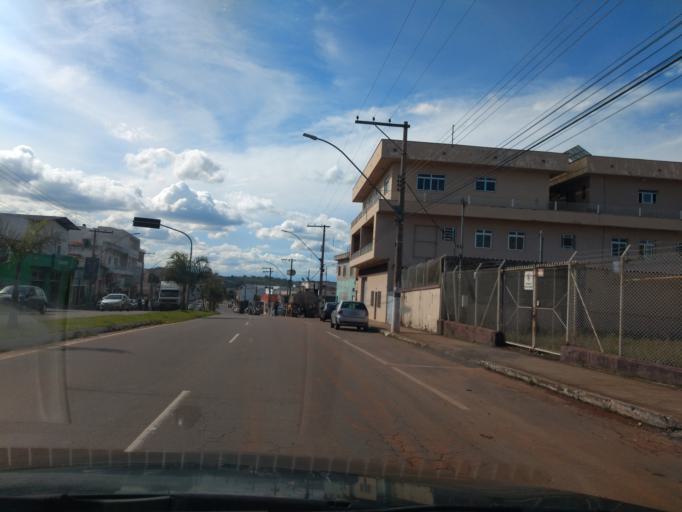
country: BR
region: Minas Gerais
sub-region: Tres Coracoes
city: Tres Coracoes
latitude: -21.6864
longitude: -45.2615
